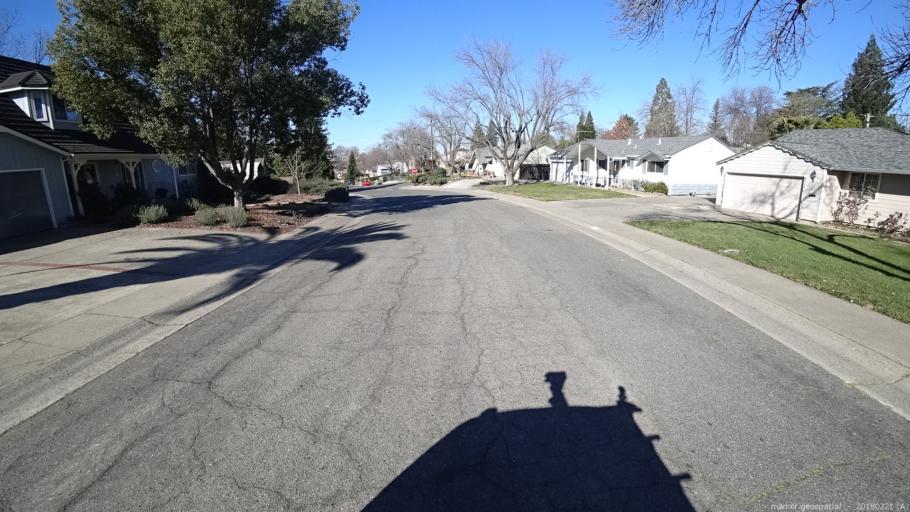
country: US
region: California
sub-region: Sacramento County
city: Orangevale
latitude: 38.6872
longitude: -121.2389
